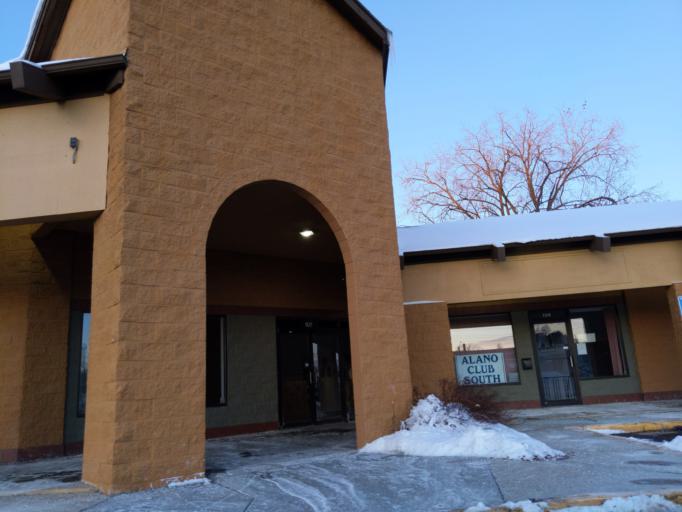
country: US
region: Michigan
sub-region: Ingham County
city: Lansing
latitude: 42.6960
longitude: -84.5488
